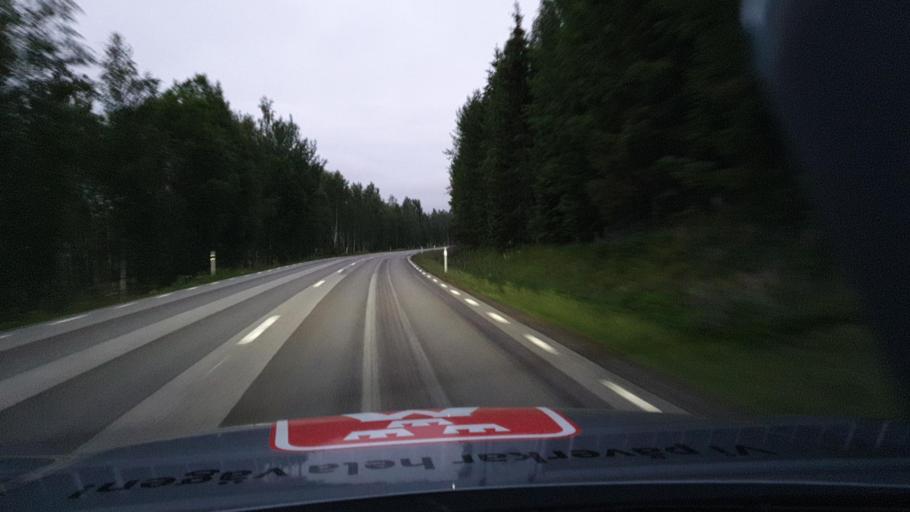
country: SE
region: OErebro
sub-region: Hallefors Kommun
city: Haellefors
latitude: 59.7840
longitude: 14.3784
